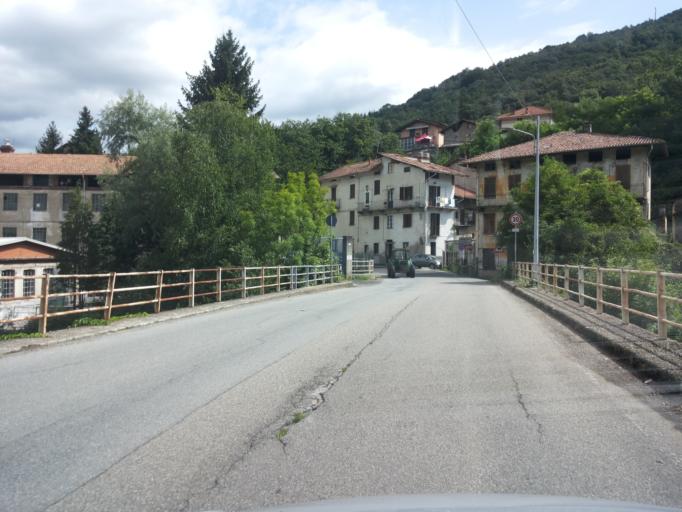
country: IT
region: Piedmont
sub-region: Provincia di Biella
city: Tollegno
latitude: 45.5985
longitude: 8.0537
